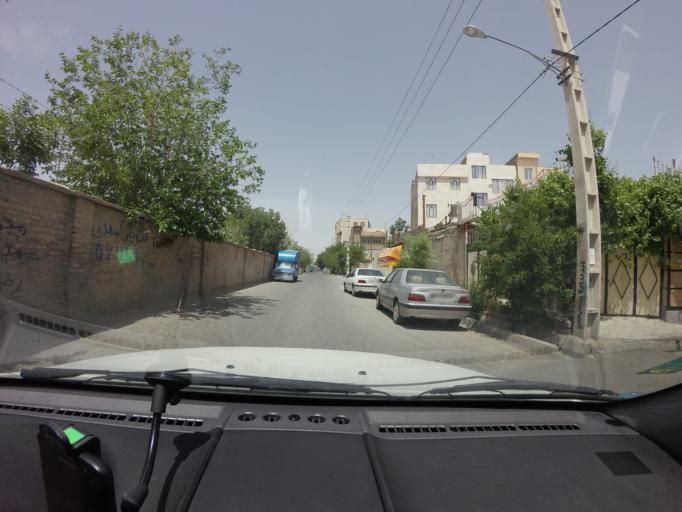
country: IR
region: Tehran
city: Eslamshahr
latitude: 35.5272
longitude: 51.2177
